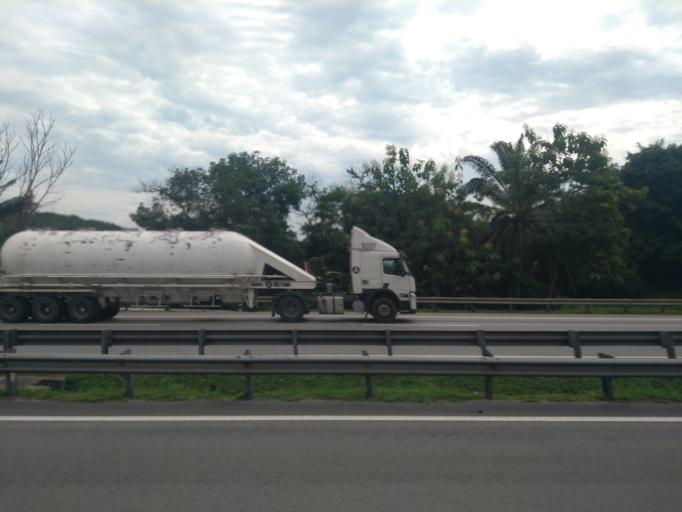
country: MY
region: Negeri Sembilan
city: Seremban
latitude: 2.6514
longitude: 101.9912
